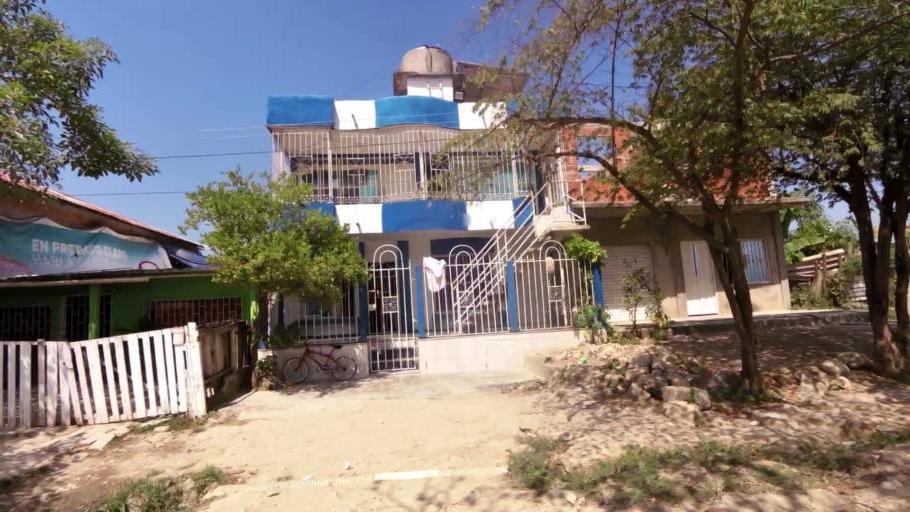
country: CO
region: Bolivar
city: Cartagena
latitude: 10.3546
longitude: -75.4838
